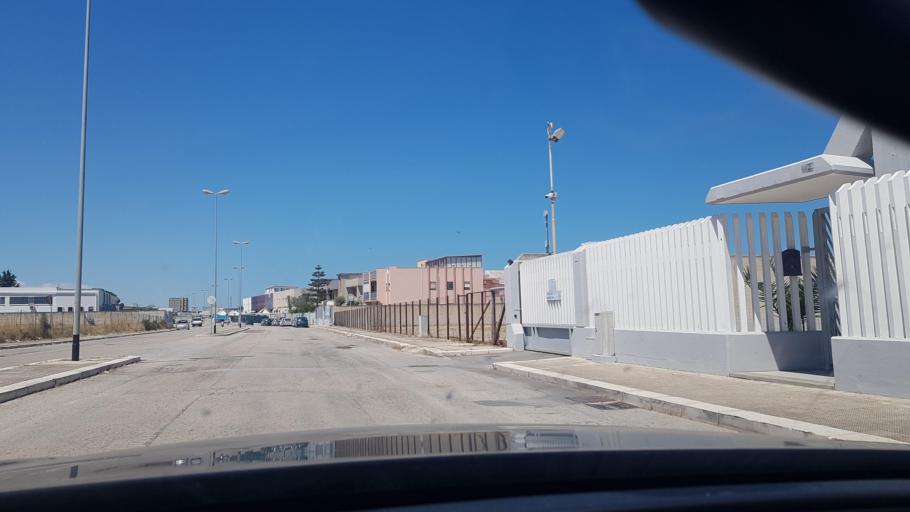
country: IT
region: Apulia
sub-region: Provincia di Barletta - Andria - Trani
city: Barletta
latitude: 41.3064
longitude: 16.3222
